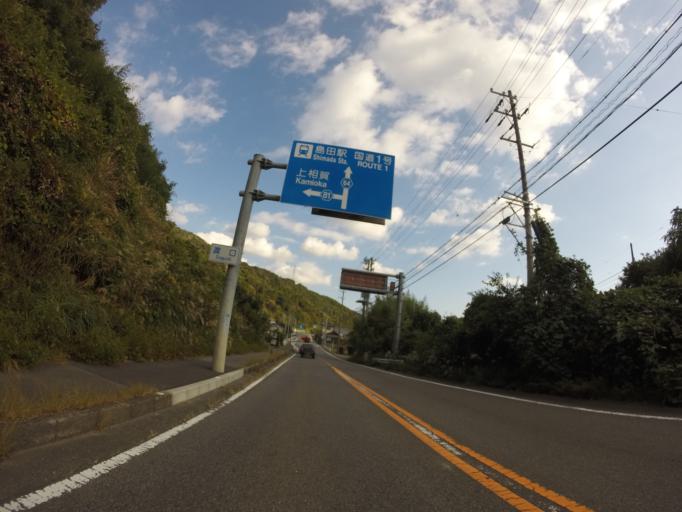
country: JP
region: Shizuoka
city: Kanaya
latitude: 34.8621
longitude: 138.1285
